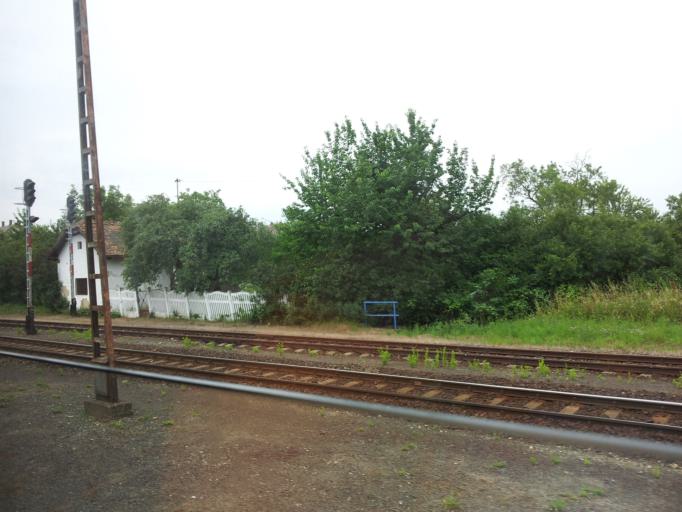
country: HU
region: Veszprem
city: Zanka
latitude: 46.8723
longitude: 17.6869
